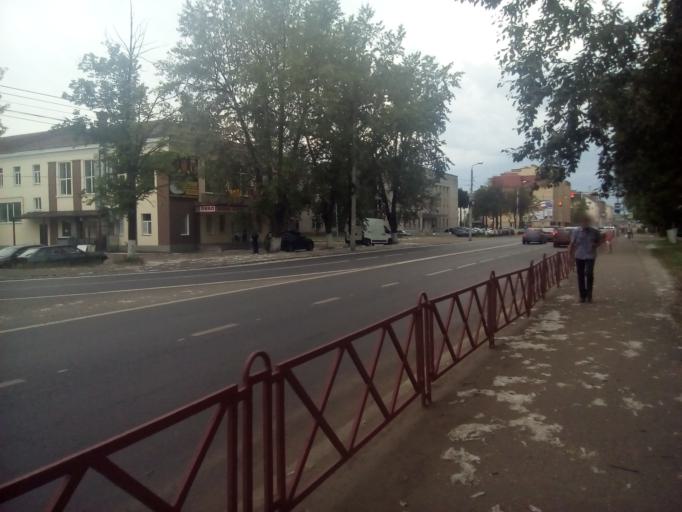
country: RU
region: Jaroslavl
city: Yaroslavl
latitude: 57.6099
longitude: 39.8737
